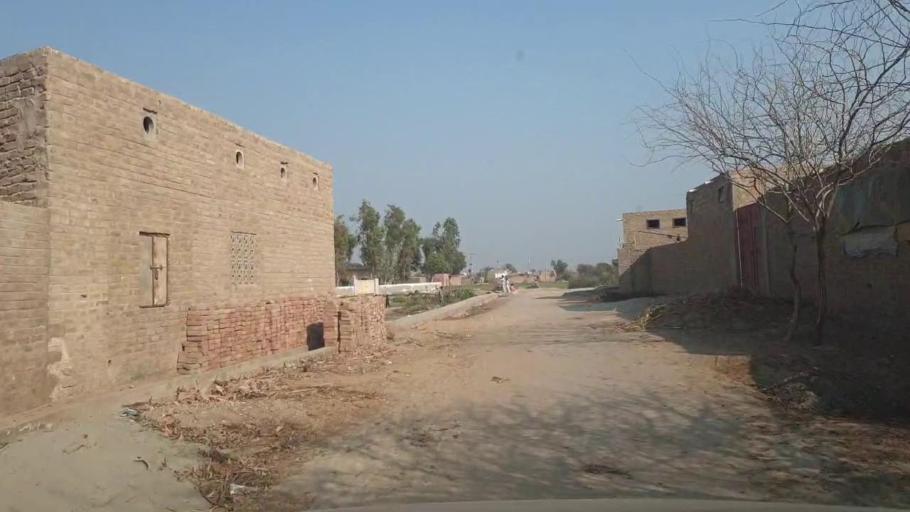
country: PK
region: Sindh
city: Tando Allahyar
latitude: 25.4387
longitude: 68.7123
